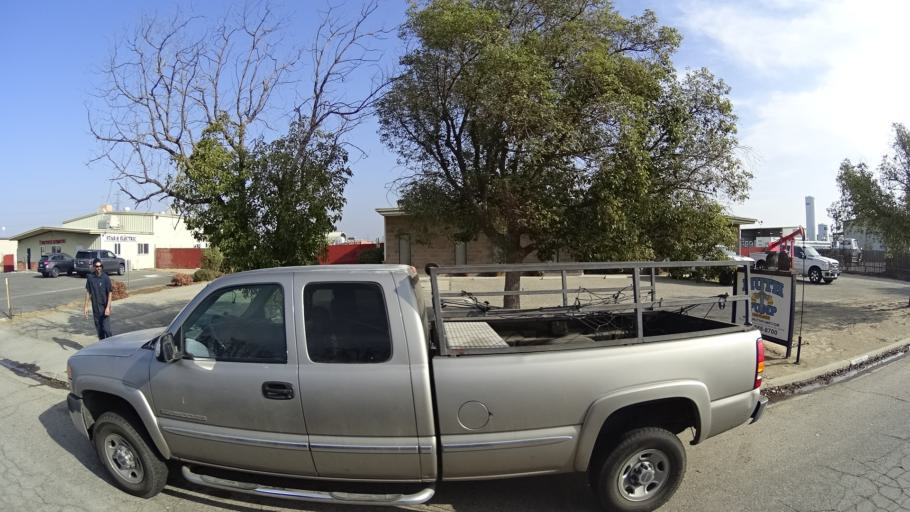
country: US
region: California
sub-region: Kern County
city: Greenacres
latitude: 35.3955
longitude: -119.0799
